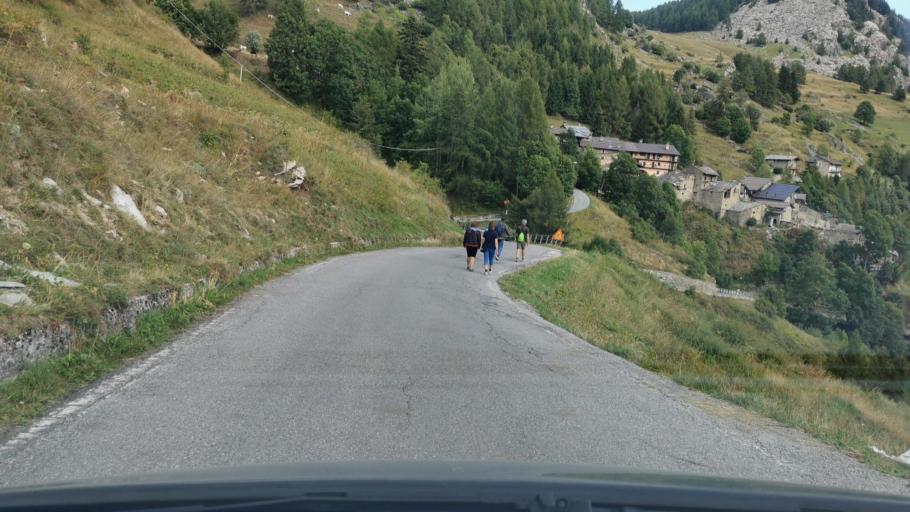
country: IT
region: Piedmont
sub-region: Provincia di Cuneo
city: Campomolino
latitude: 44.3996
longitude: 7.1719
